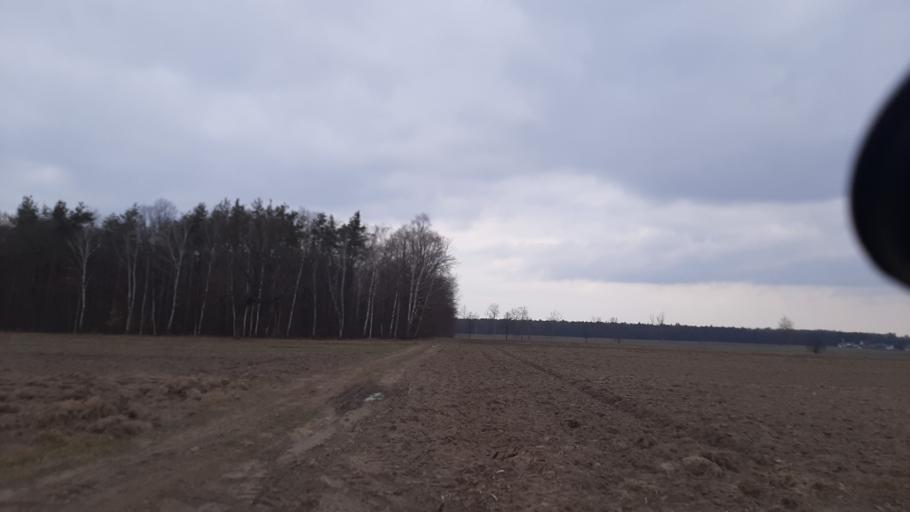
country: PL
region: Lublin Voivodeship
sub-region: Powiat lubelski
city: Garbow
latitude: 51.3853
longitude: 22.4066
